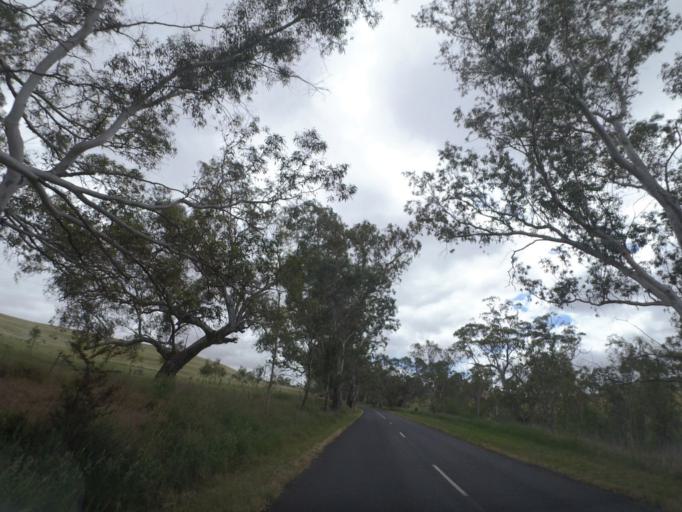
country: AU
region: Victoria
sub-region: Whittlesea
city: Whittlesea
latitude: -37.1944
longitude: 145.0382
